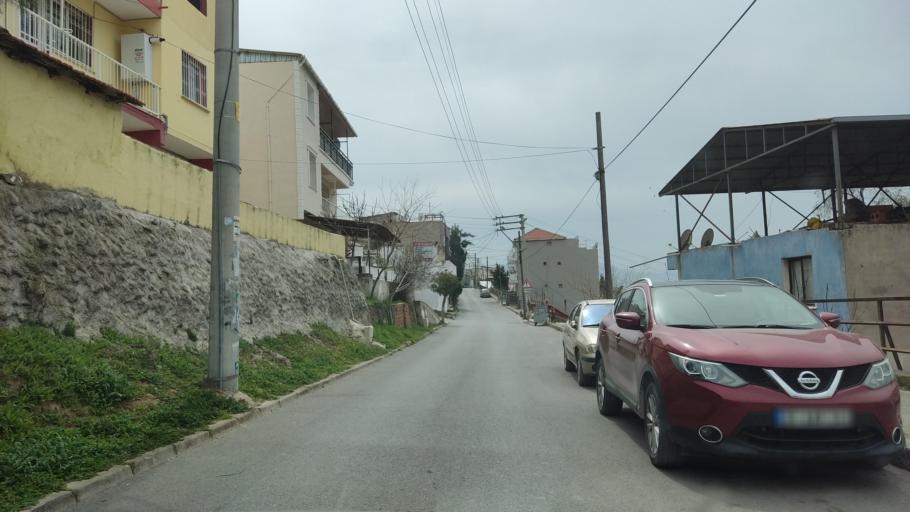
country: TR
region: Izmir
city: Karsiyaka
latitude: 38.4991
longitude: 27.0719
